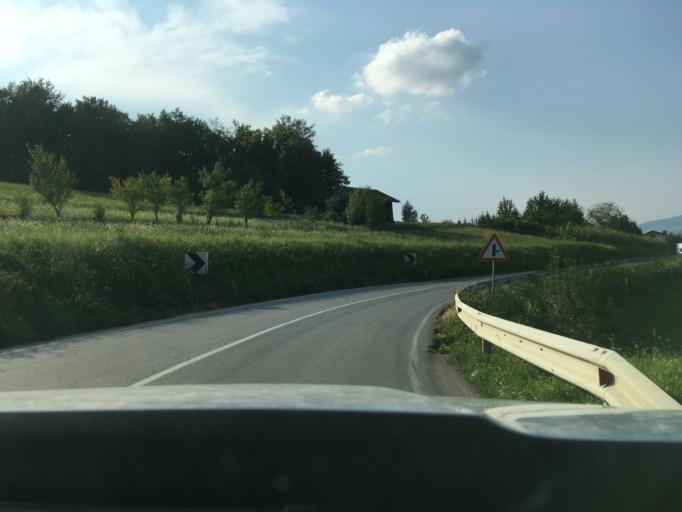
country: SI
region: Novo Mesto
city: Novo Mesto
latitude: 45.7707
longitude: 15.1913
